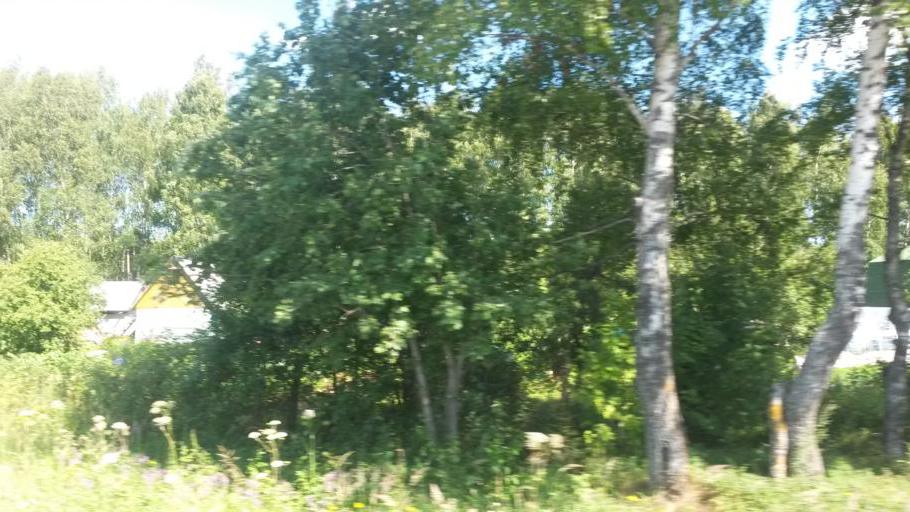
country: RU
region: Jaroslavl
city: Krasnyye Tkachi
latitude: 57.4631
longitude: 39.9087
